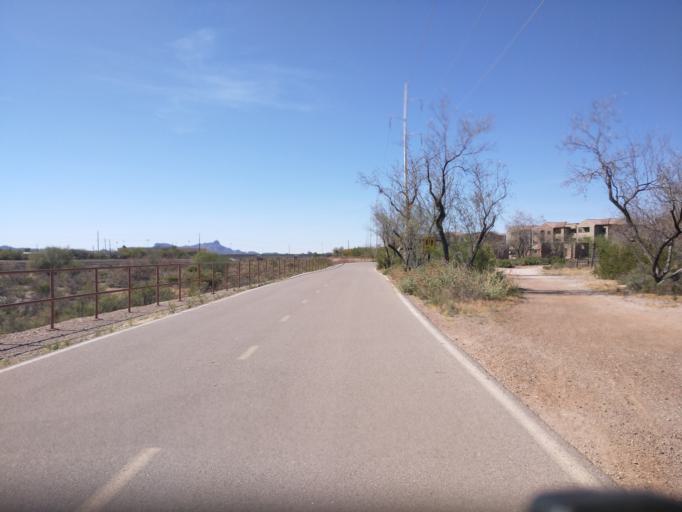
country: US
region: Arizona
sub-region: Pima County
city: Flowing Wells
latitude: 32.3005
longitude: -111.0071
